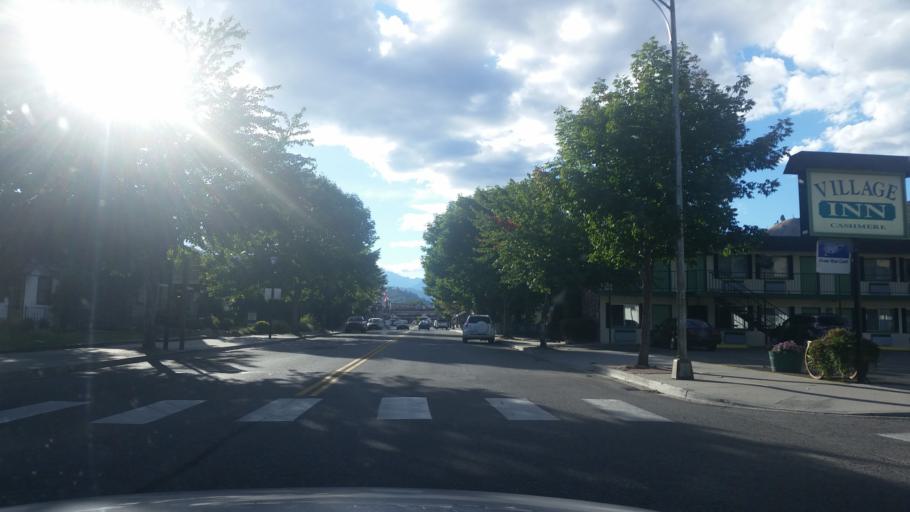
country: US
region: Washington
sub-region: Chelan County
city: Cashmere
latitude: 47.5215
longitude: -120.4653
